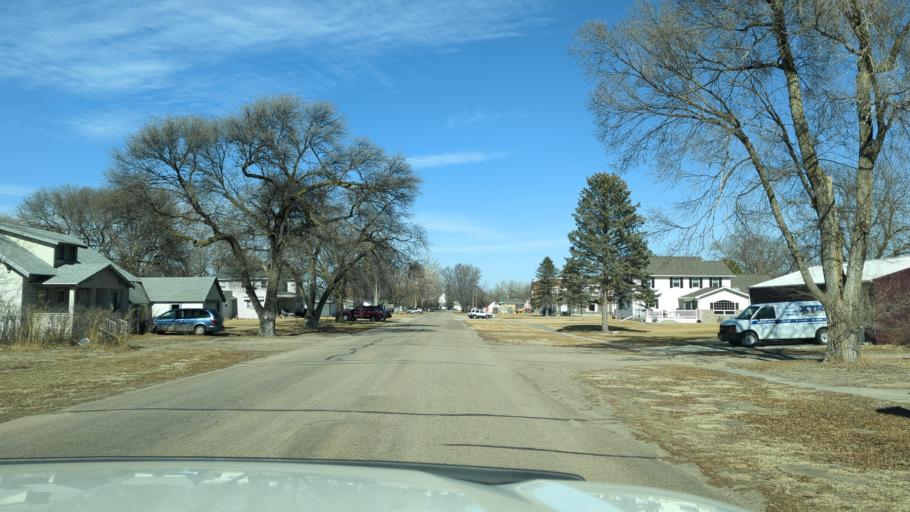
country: US
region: Nebraska
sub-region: Antelope County
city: Neligh
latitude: 42.2591
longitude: -98.3451
